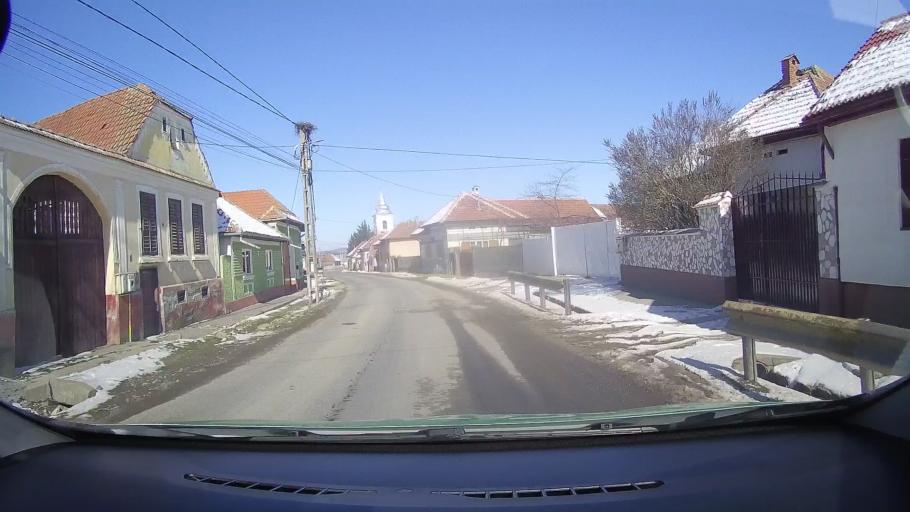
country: RO
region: Brasov
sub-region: Oras Victoria
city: Victoria
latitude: 45.7453
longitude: 24.7401
